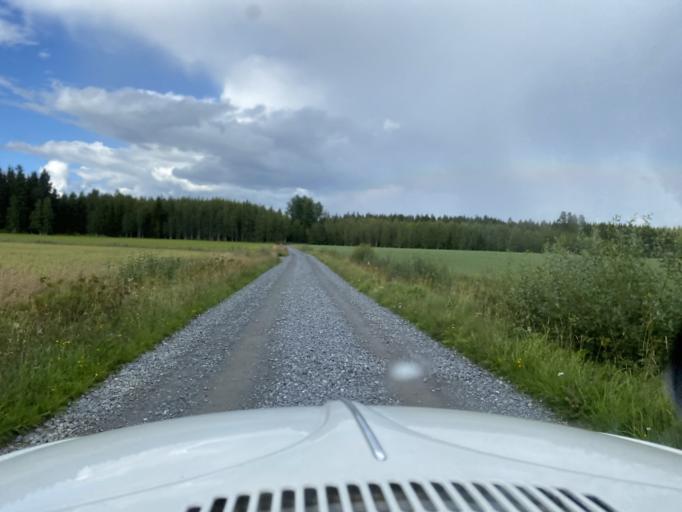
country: FI
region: Pirkanmaa
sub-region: Lounais-Pirkanmaa
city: Punkalaidun
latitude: 61.1330
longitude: 23.0670
